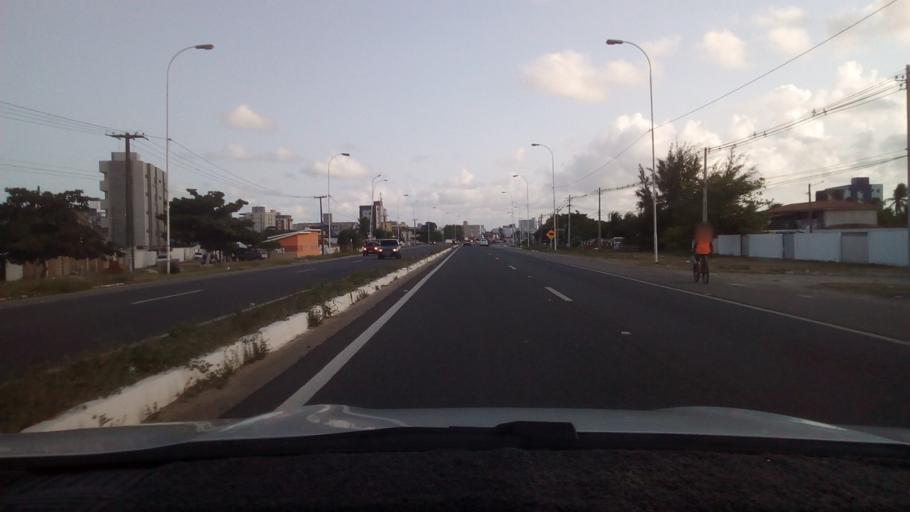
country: BR
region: Paraiba
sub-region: Cabedelo
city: Cabedelo
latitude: -6.9995
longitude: -34.8284
